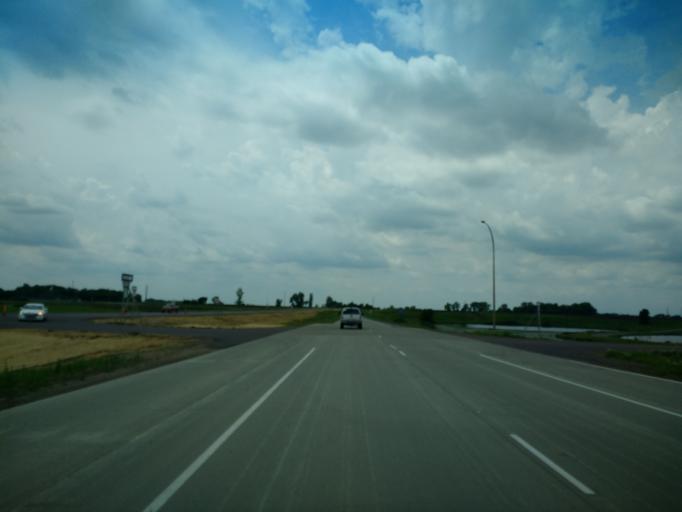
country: US
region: Minnesota
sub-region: Cottonwood County
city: Windom
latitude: 43.9071
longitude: -95.0567
